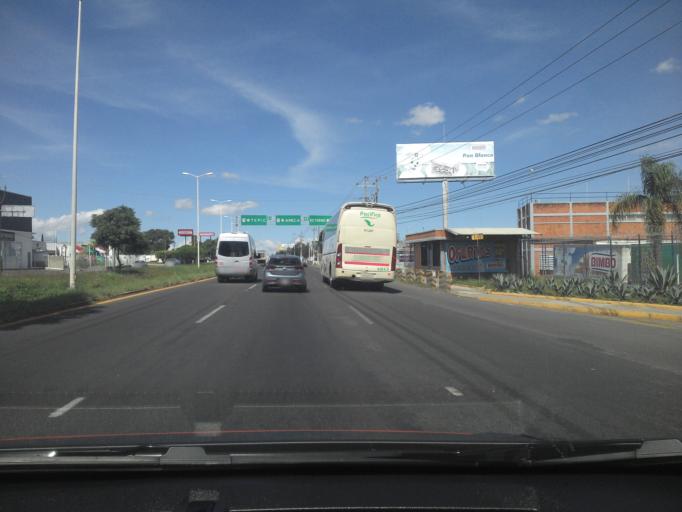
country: MX
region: Jalisco
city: Nuevo Mexico
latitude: 20.7071
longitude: -103.4647
